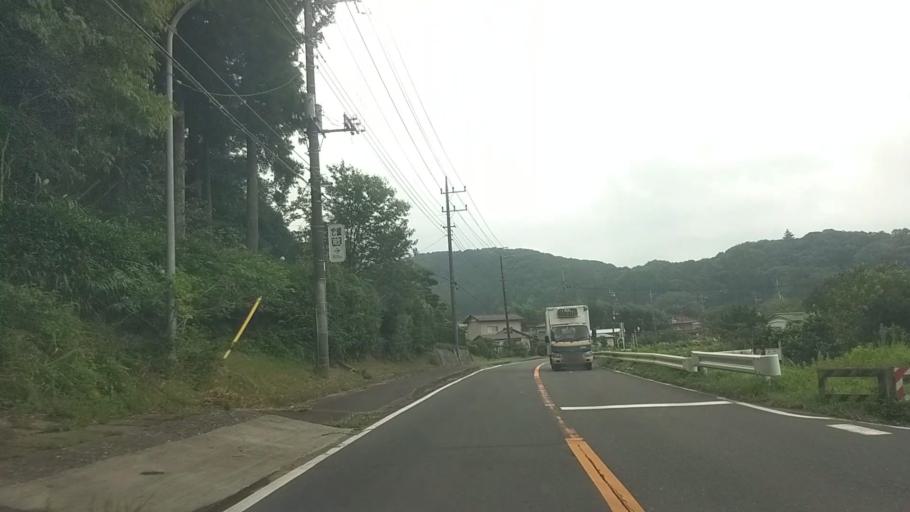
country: JP
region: Chiba
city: Kawaguchi
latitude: 35.2612
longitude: 140.0625
